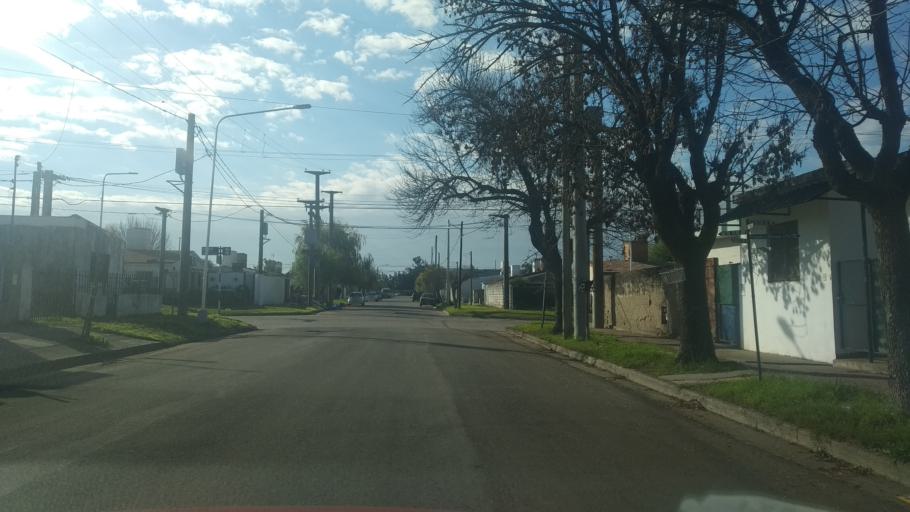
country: AR
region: Cordoba
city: Leones
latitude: -32.6576
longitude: -62.2933
